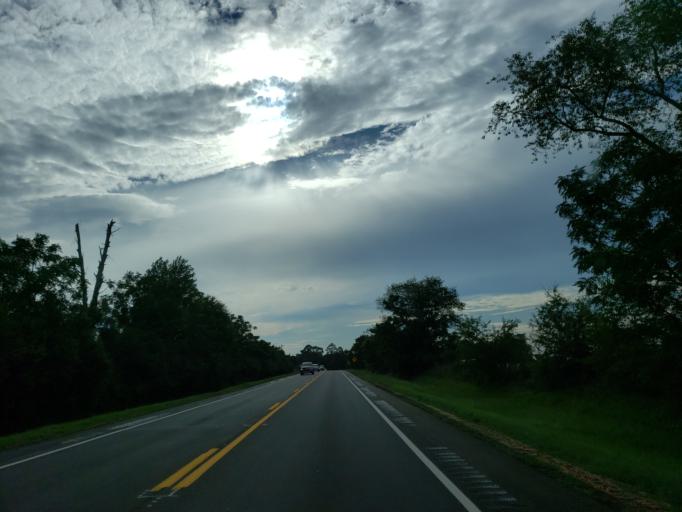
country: US
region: Georgia
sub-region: Irwin County
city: Ocilla
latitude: 31.5643
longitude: -83.3356
